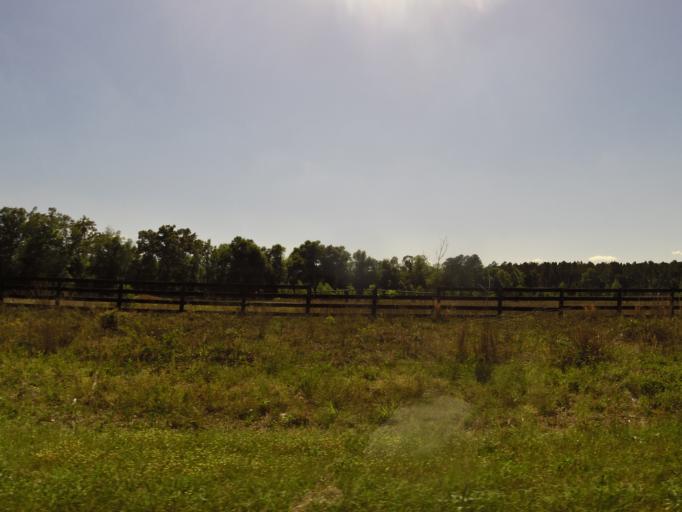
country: US
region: South Carolina
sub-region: Barnwell County
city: Williston
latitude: 33.4296
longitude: -81.4819
